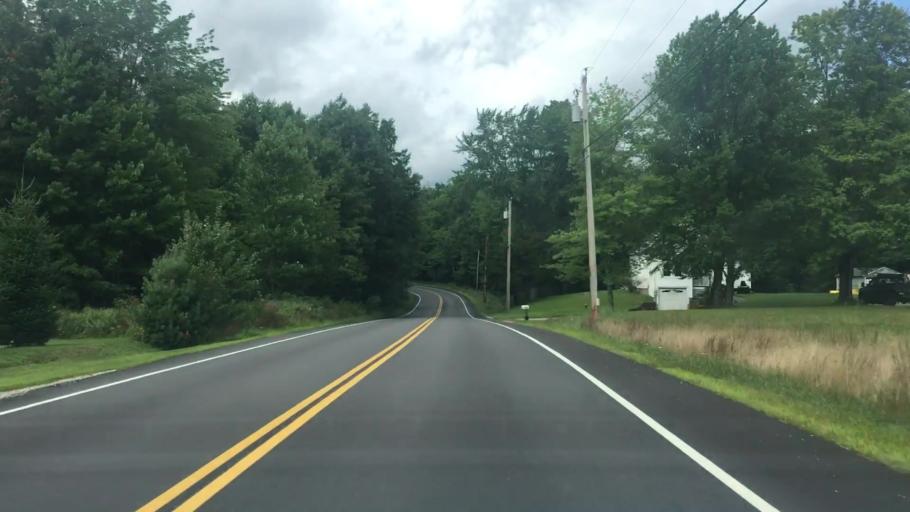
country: US
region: Maine
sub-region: York County
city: West Kennebunk
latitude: 43.4716
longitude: -70.6013
